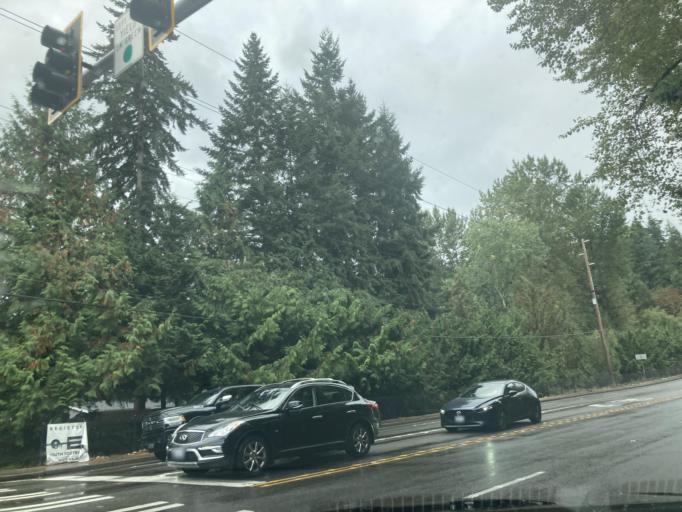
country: US
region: Washington
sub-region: Pierce County
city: South Hill
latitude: 47.1547
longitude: -122.2672
